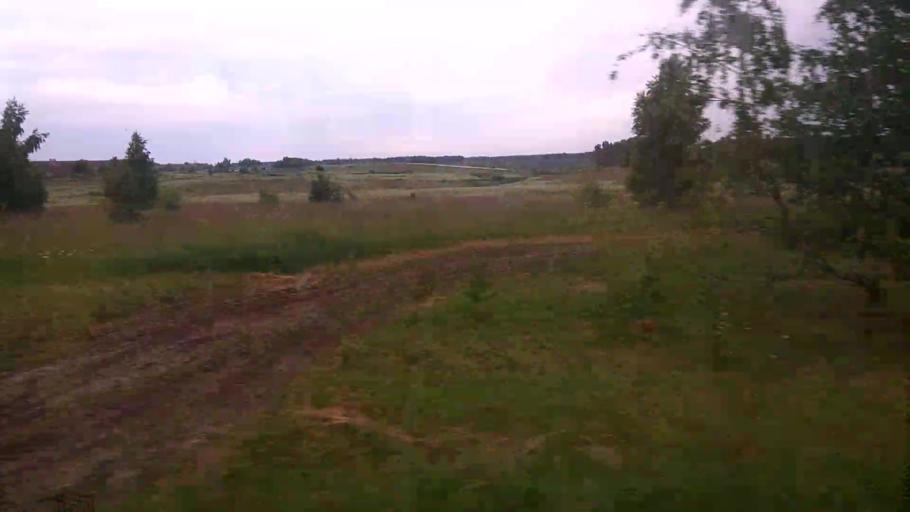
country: RU
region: Moskovskaya
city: Ozery
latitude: 54.7708
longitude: 38.6523
